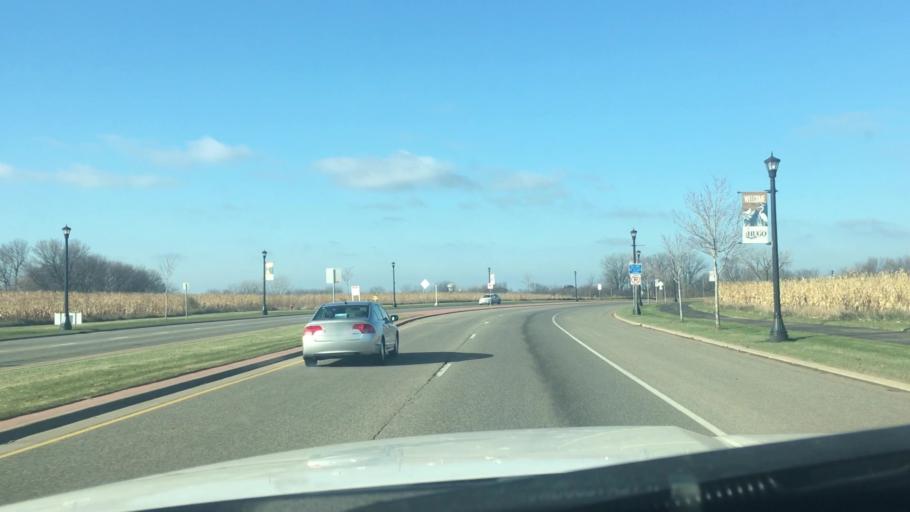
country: US
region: Minnesota
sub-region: Washington County
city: Hugo
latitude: 45.1575
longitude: -92.9957
